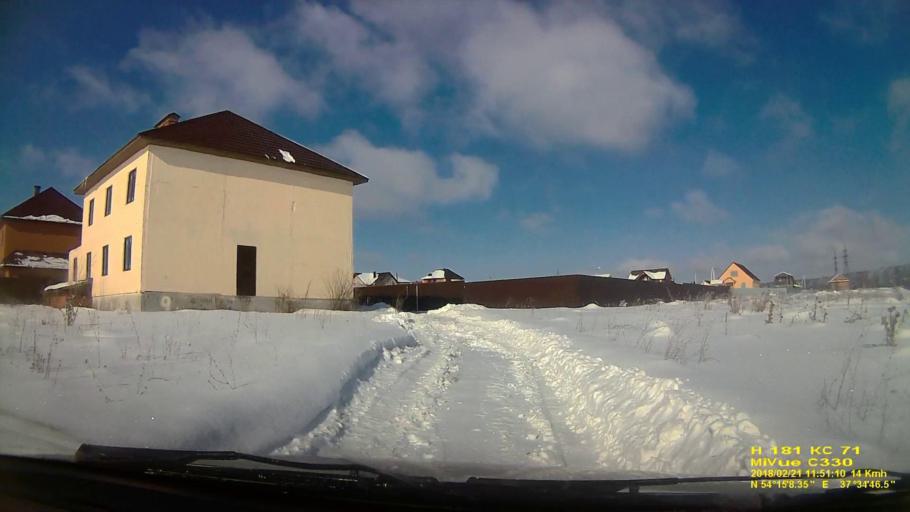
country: RU
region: Tula
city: Gorelki
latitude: 54.2523
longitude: 37.5796
